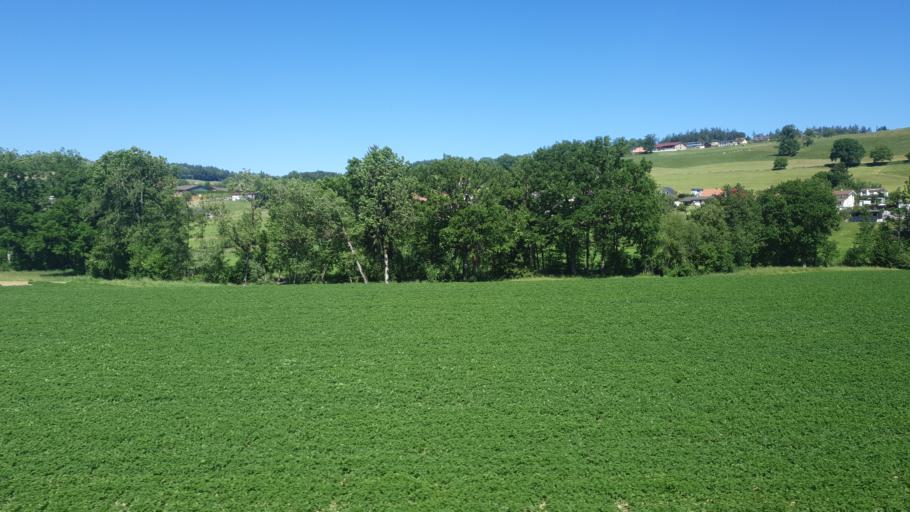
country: CH
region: Fribourg
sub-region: Sarine District
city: Givisiez
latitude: 46.8321
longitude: 7.1247
